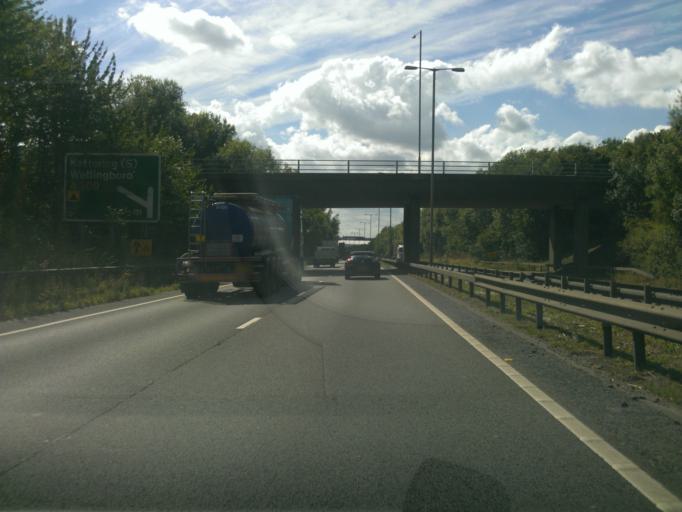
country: GB
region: England
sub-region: Northamptonshire
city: Burton Latimer
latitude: 52.3739
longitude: -0.6930
